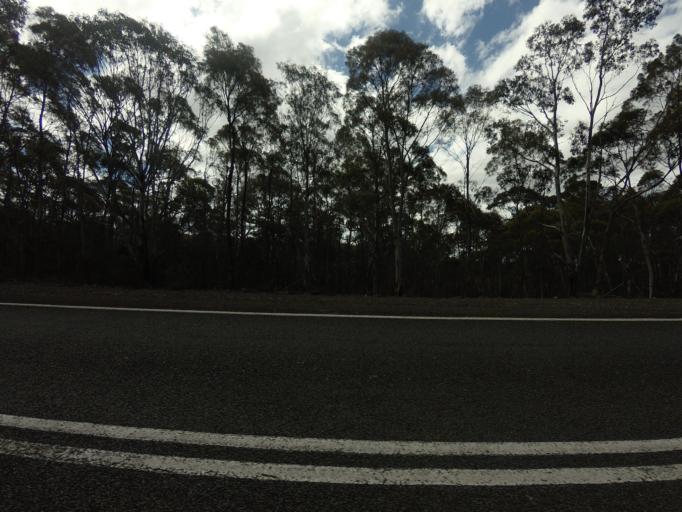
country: AU
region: Tasmania
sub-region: Break O'Day
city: St Helens
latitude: -42.0133
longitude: 147.9268
